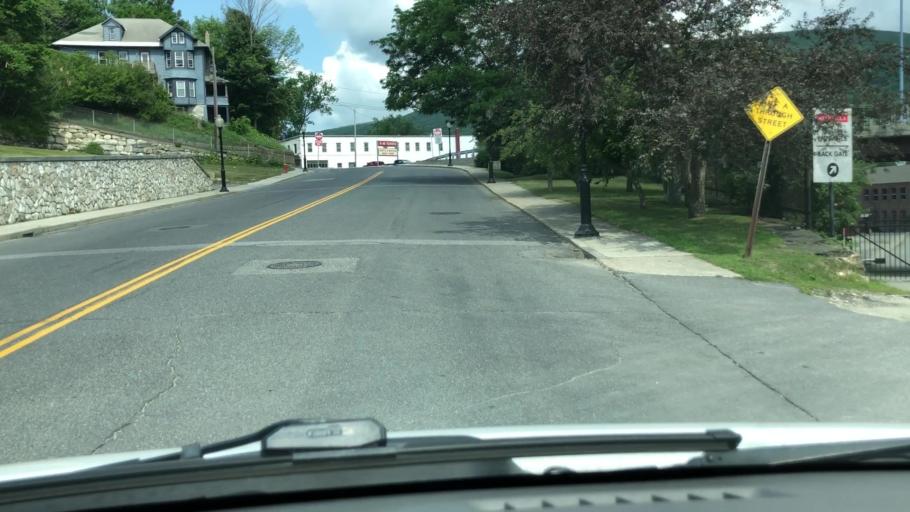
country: US
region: Massachusetts
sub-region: Berkshire County
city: North Adams
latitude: 42.6999
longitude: -73.1148
